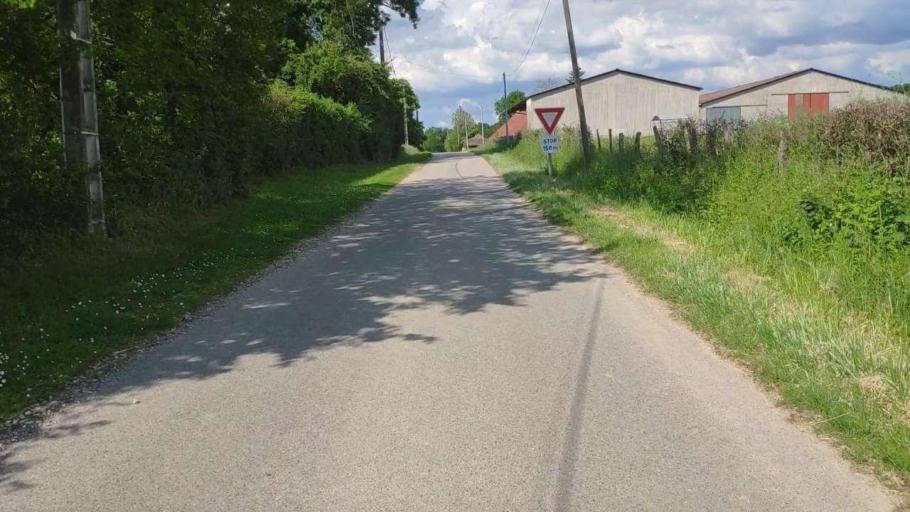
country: FR
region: Franche-Comte
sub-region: Departement du Jura
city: Bletterans
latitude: 46.8283
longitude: 5.4078
